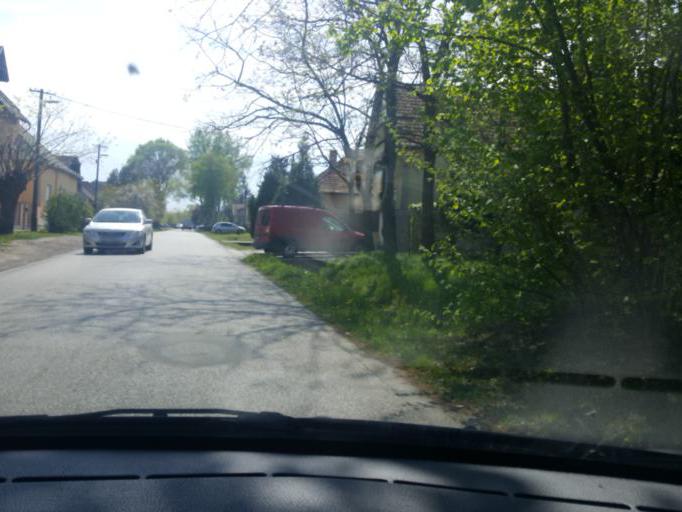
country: HU
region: Pest
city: Monor
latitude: 47.3501
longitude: 19.4404
